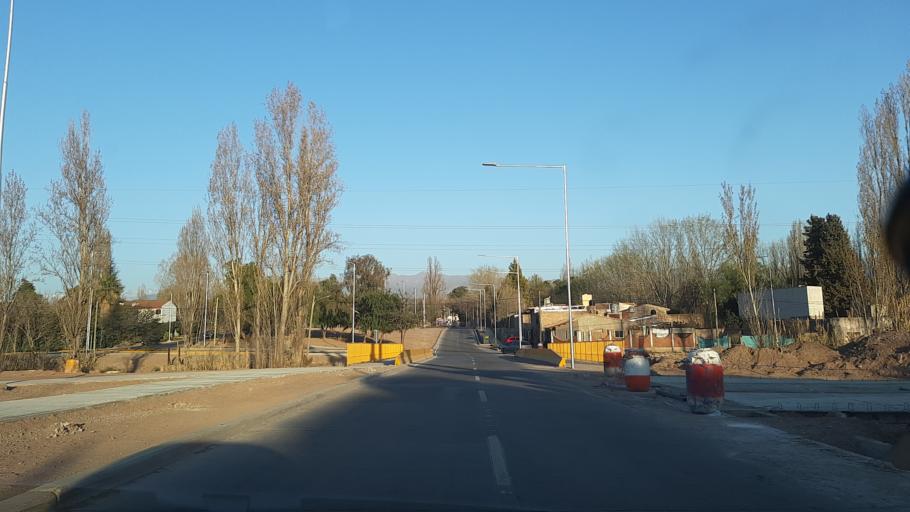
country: AR
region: Mendoza
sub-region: Departamento de Godoy Cruz
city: Godoy Cruz
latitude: -32.9651
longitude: -68.8556
